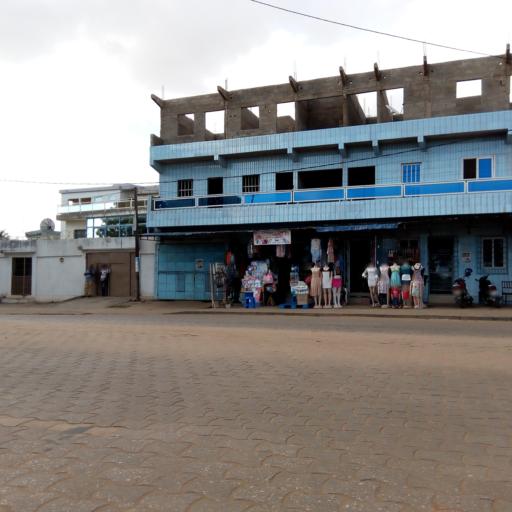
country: TG
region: Maritime
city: Lome
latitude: 6.1625
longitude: 1.2127
